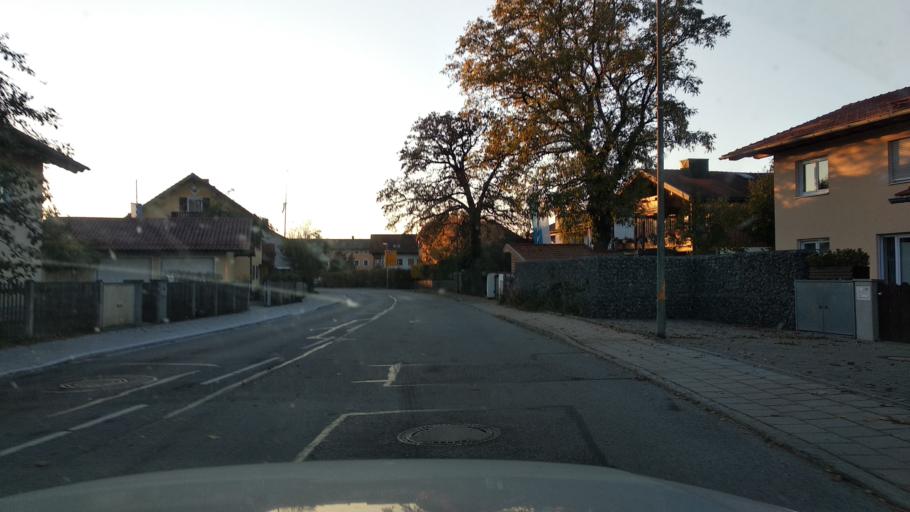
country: DE
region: Bavaria
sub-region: Upper Bavaria
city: Hohenkirchen-Siegertsbrunn
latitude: 48.0200
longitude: 11.7316
